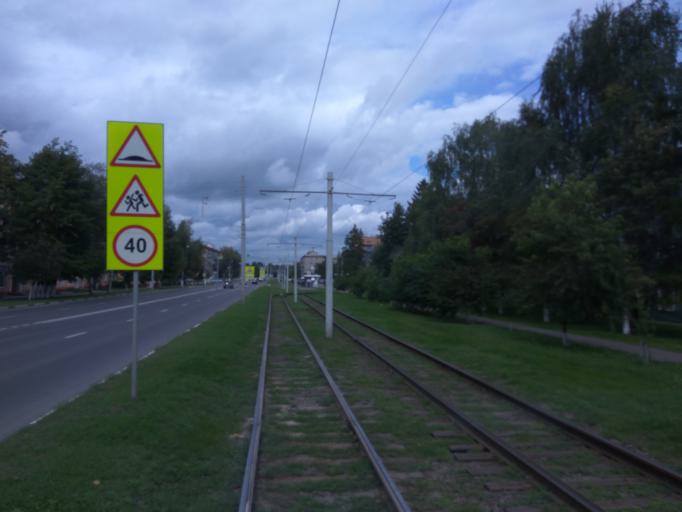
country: RU
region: Moskovskaya
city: Kolomna
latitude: 55.0890
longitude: 38.7663
